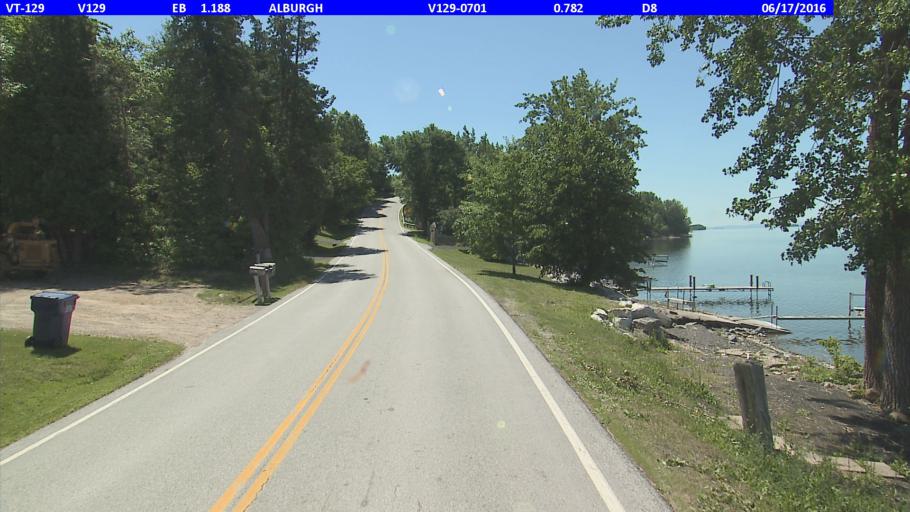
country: US
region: Vermont
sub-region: Grand Isle County
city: North Hero
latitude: 44.9001
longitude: -73.3042
